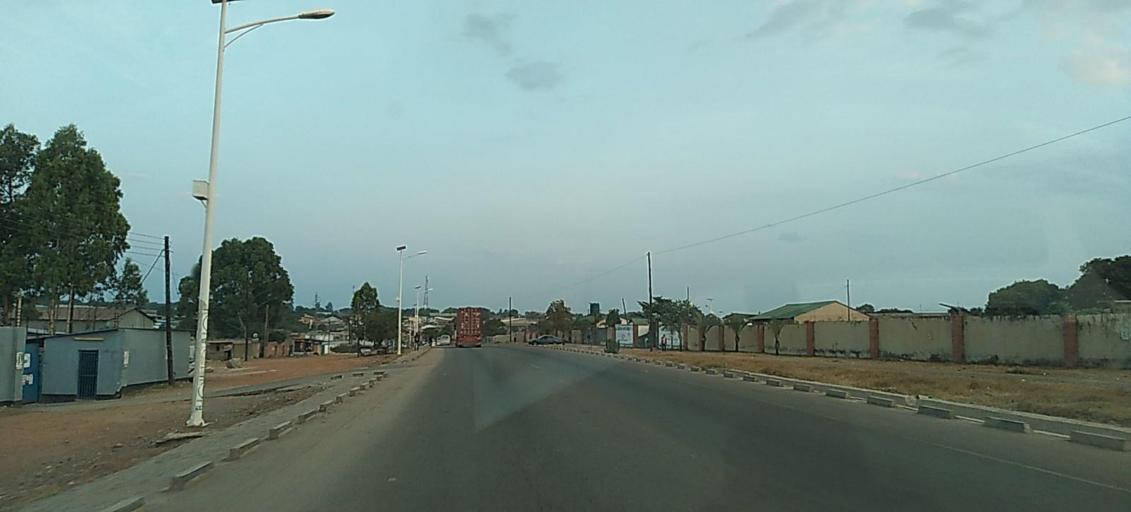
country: ZM
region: Copperbelt
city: Chingola
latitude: -12.5428
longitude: 27.8458
